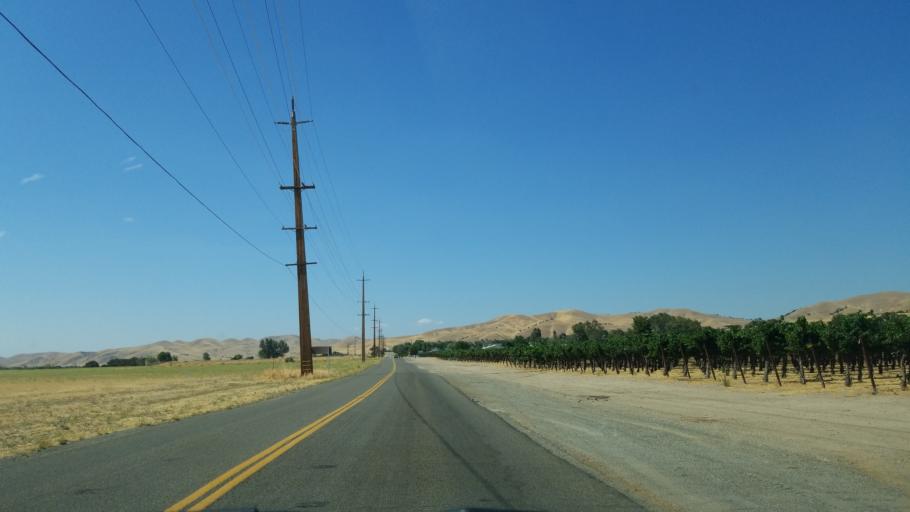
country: US
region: California
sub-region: San Luis Obispo County
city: San Miguel
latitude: 35.7368
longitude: -120.6853
